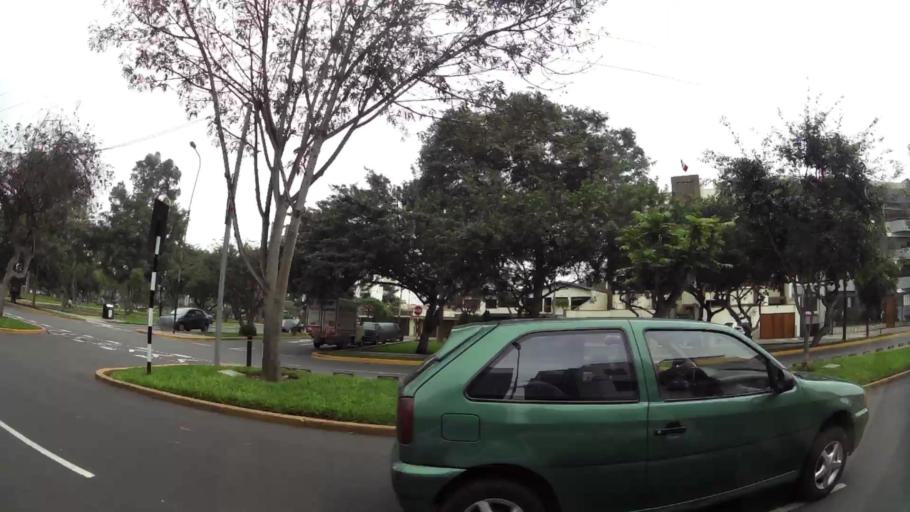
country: PE
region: Lima
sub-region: Lima
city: Surco
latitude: -12.1141
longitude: -76.9790
